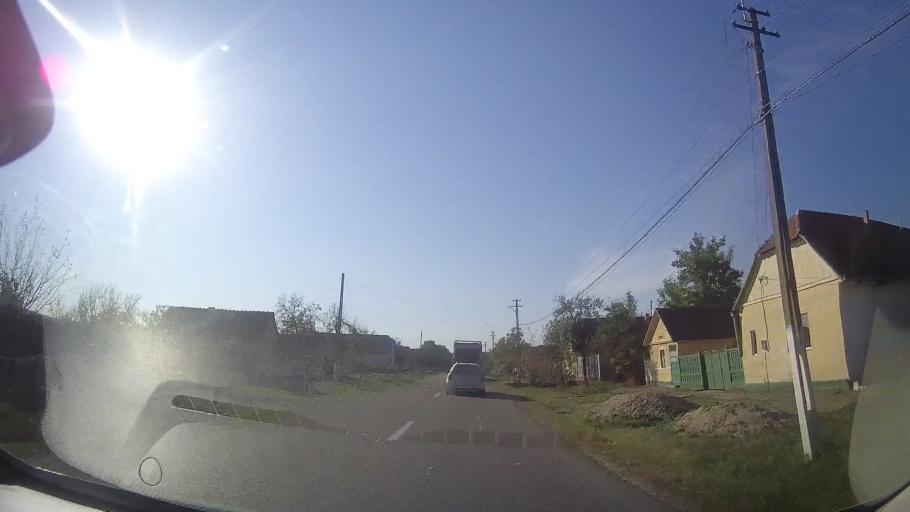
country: RO
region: Timis
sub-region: Oras Recas
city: Recas
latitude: 45.8543
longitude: 21.5160
